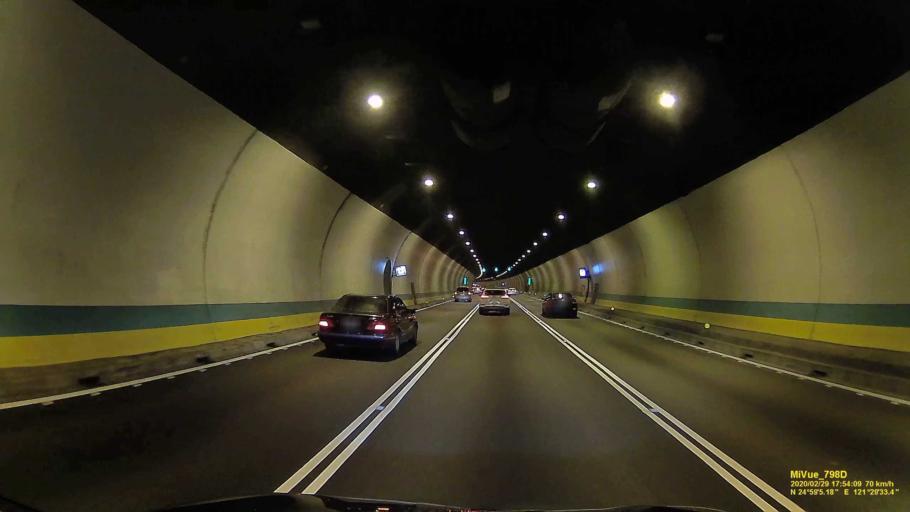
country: TW
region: Taipei
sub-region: Taipei
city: Banqiao
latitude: 24.9843
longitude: 121.4931
